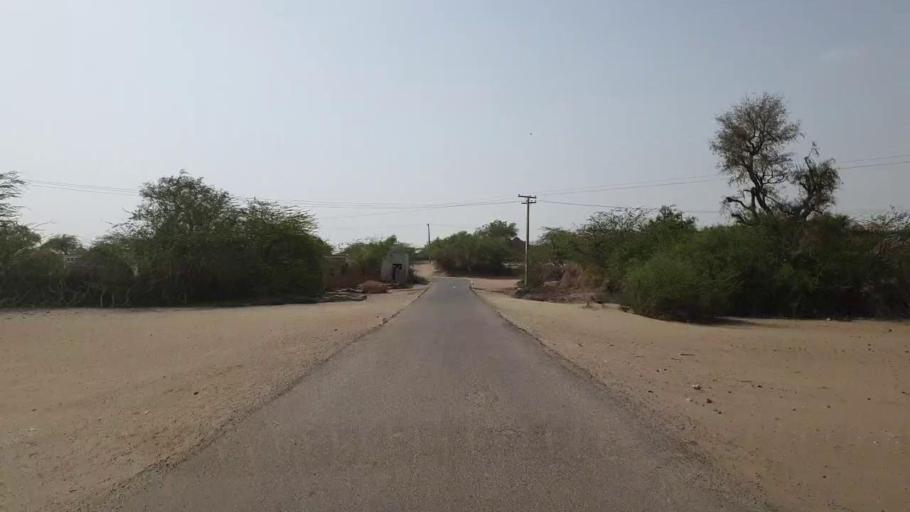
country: PK
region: Sindh
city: Mithi
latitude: 24.5755
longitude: 69.9289
